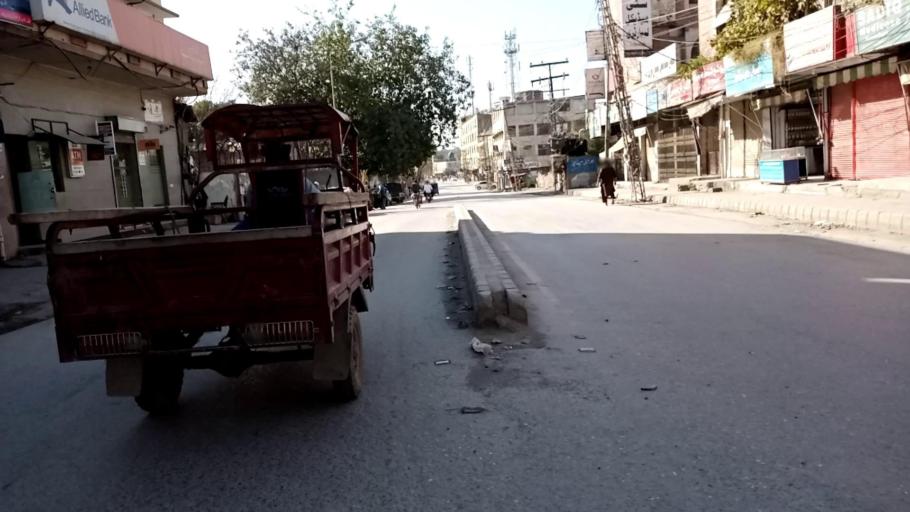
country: PK
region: Khyber Pakhtunkhwa
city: Peshawar
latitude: 34.0036
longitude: 71.5601
